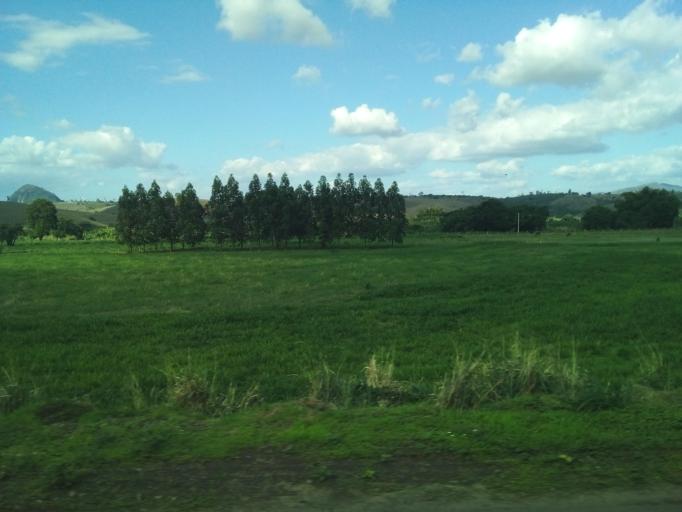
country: BR
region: Minas Gerais
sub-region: Conselheiro Pena
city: Conselheiro Pena
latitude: -18.9925
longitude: -41.5976
